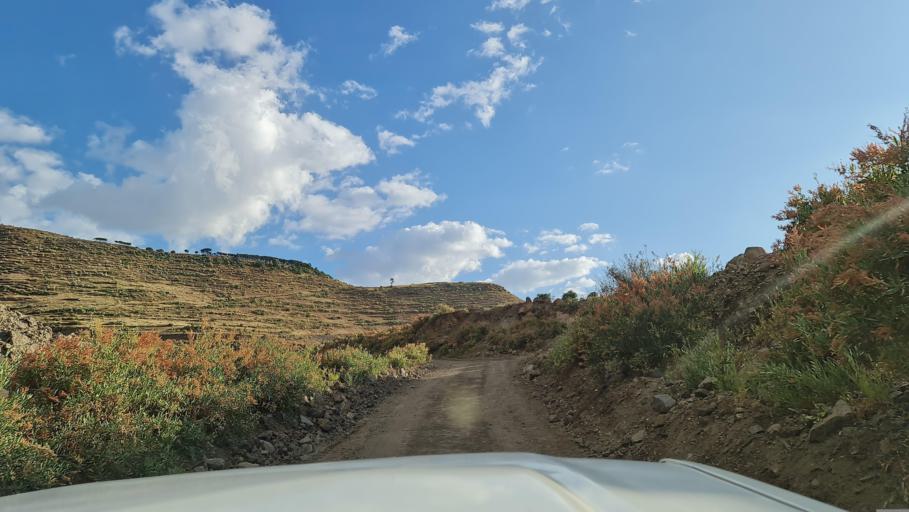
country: ET
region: Amhara
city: Debark'
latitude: 13.0508
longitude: 38.0196
